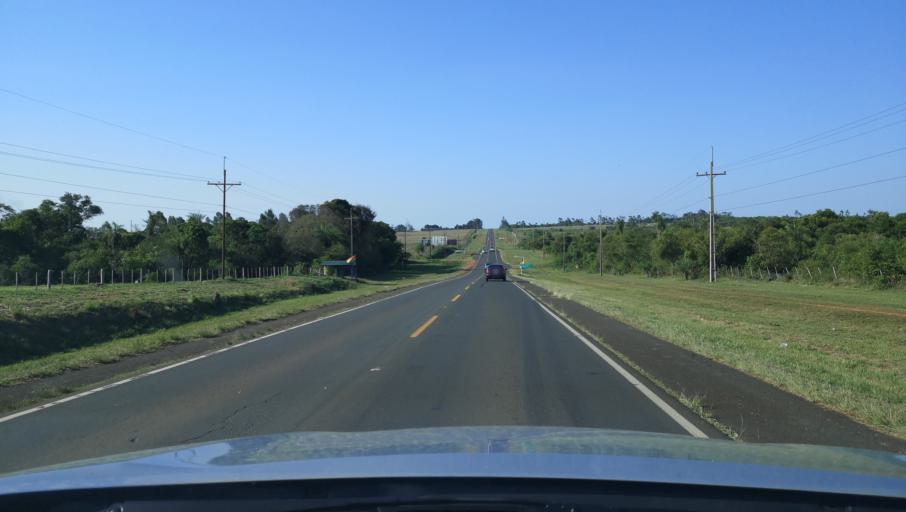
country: PY
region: Misiones
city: Santa Maria
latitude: -26.8350
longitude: -57.0333
